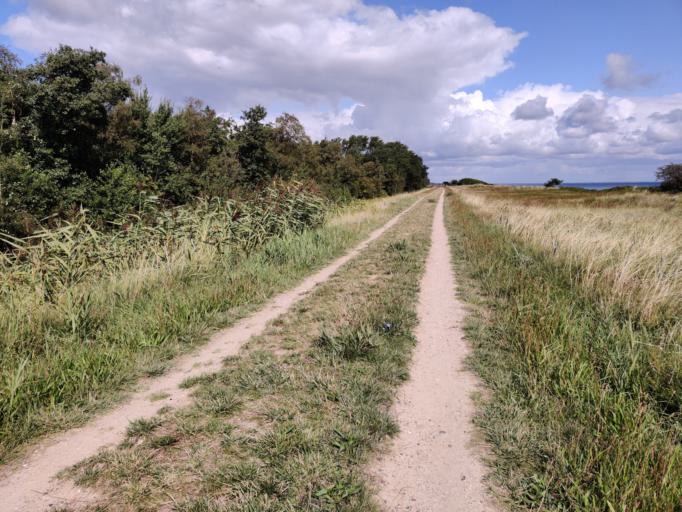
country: DK
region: Zealand
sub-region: Guldborgsund Kommune
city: Nykobing Falster
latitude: 54.5869
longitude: 11.9710
